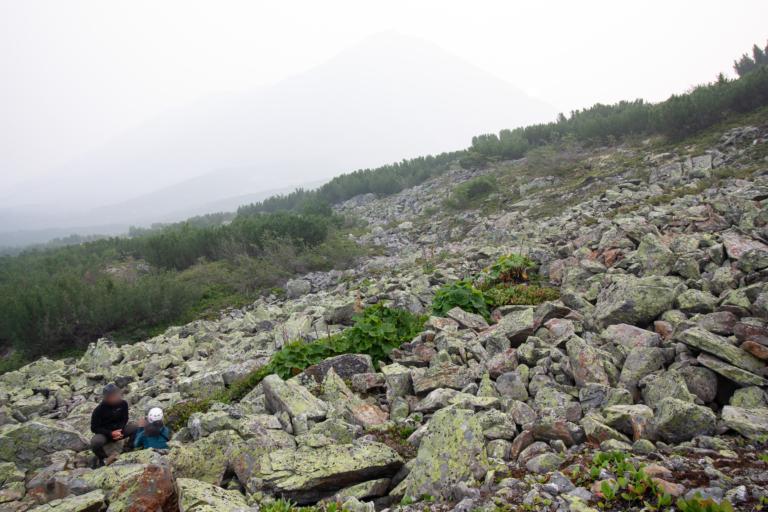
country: RU
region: Respublika Buryatiya
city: Kichera
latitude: 56.2375
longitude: 110.5960
